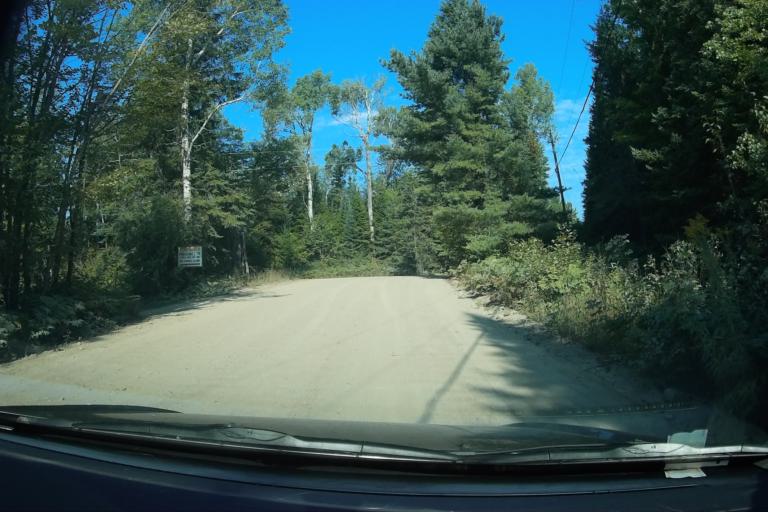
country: CA
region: Ontario
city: Huntsville
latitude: 45.5639
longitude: -78.7042
